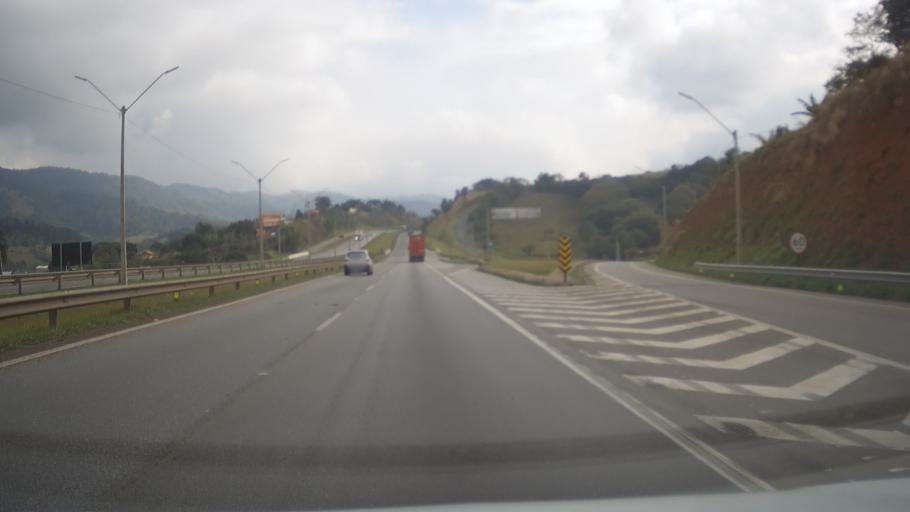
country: BR
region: Minas Gerais
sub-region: Extrema
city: Extrema
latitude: -22.9000
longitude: -46.4198
